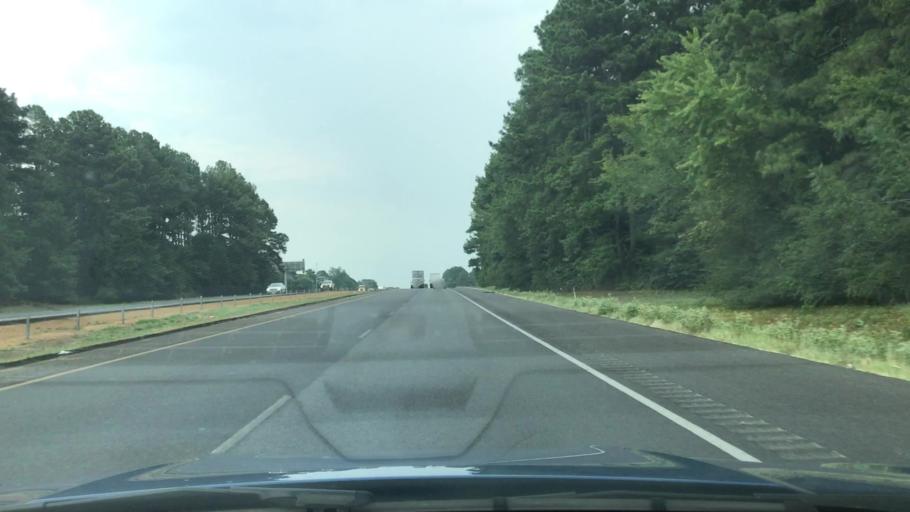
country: US
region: Texas
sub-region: Harrison County
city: Marshall
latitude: 32.4946
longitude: -94.2712
